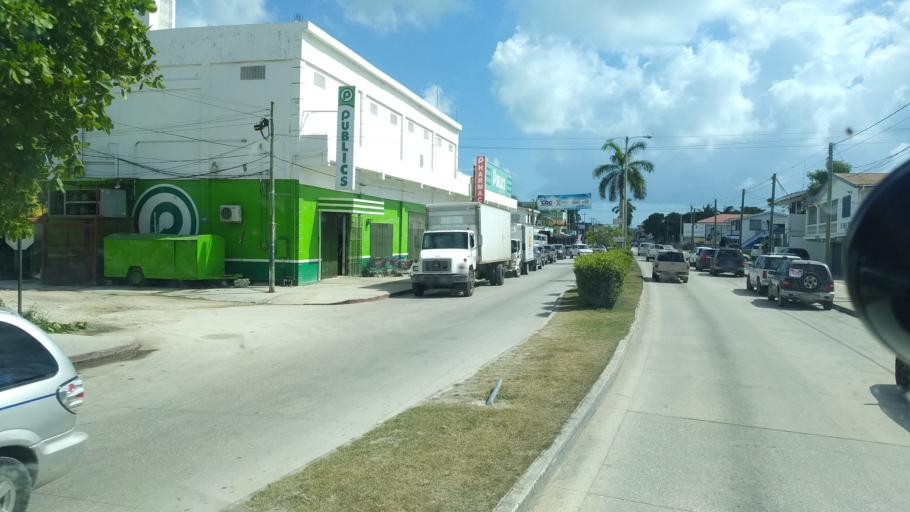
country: BZ
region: Belize
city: Belize City
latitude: 17.4998
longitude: -88.1990
